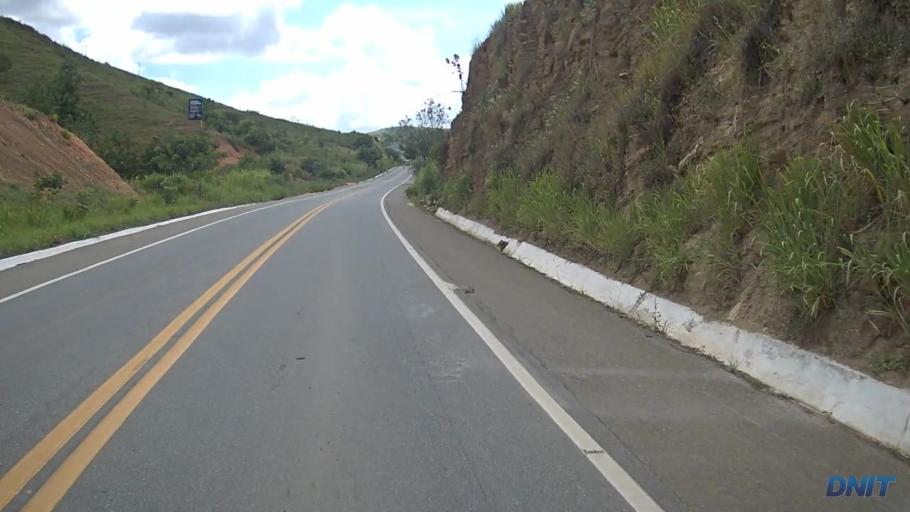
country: BR
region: Minas Gerais
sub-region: Governador Valadares
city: Governador Valadares
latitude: -18.9293
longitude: -42.0438
